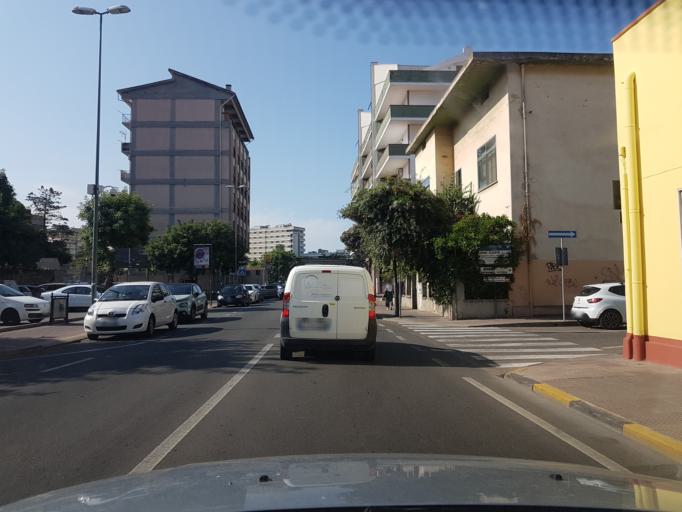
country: IT
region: Sardinia
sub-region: Provincia di Oristano
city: Oristano
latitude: 39.9043
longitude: 8.5884
